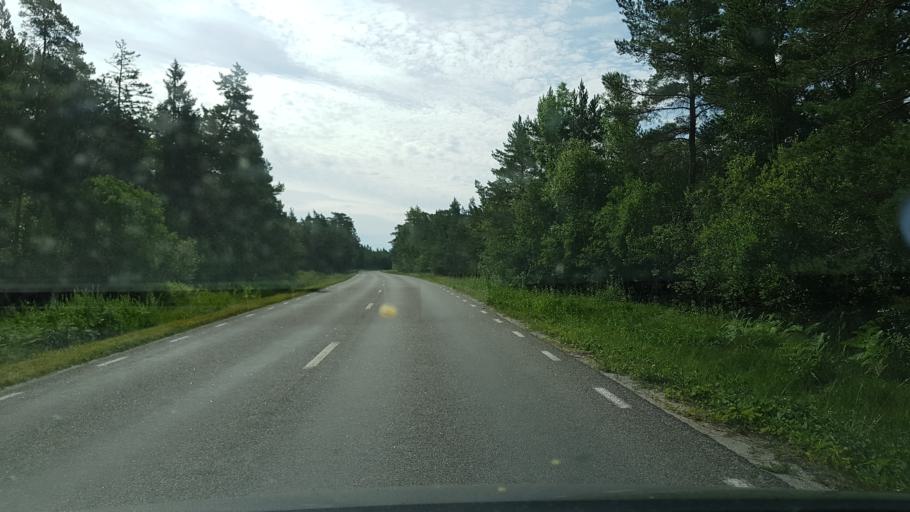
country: SE
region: Gotland
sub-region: Gotland
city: Hemse
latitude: 57.4516
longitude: 18.5814
